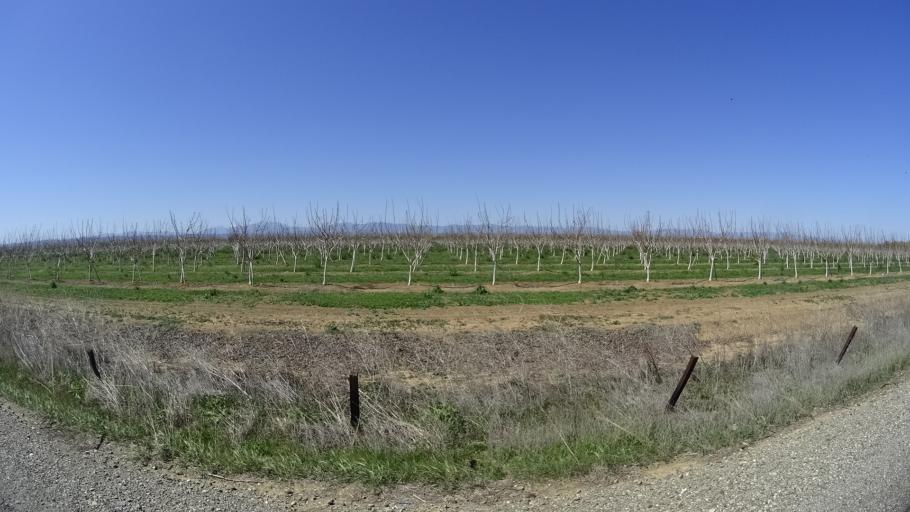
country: US
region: California
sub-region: Glenn County
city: Willows
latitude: 39.5696
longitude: -122.2496
